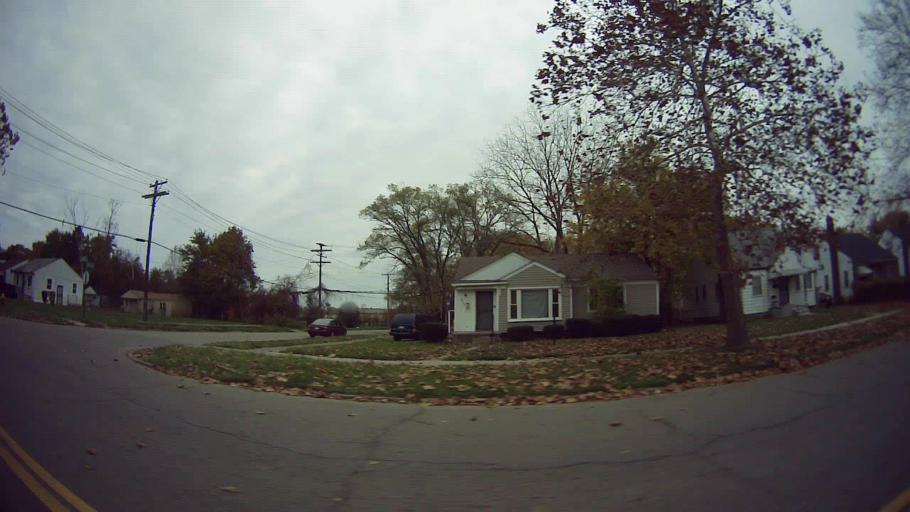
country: US
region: Michigan
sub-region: Wayne County
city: Dearborn
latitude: 42.3539
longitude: -83.1870
